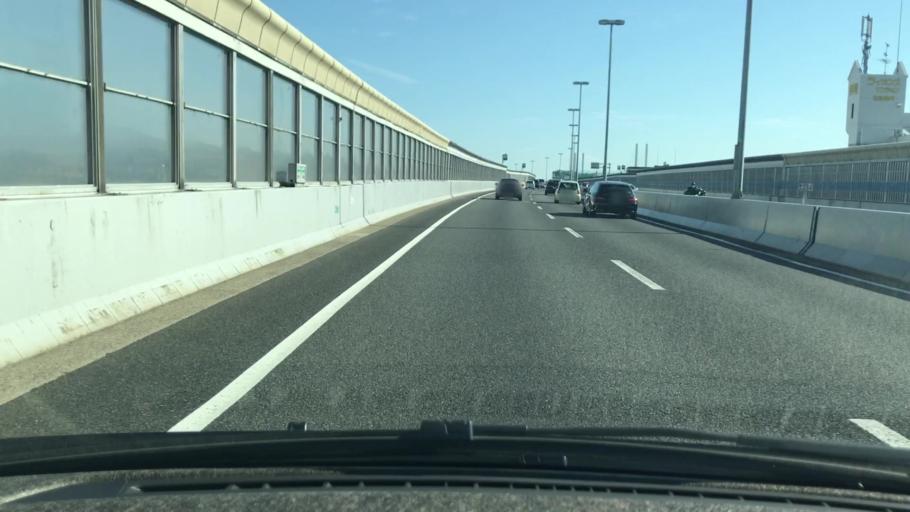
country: JP
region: Hyogo
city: Ashiya
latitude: 34.7113
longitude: 135.2661
